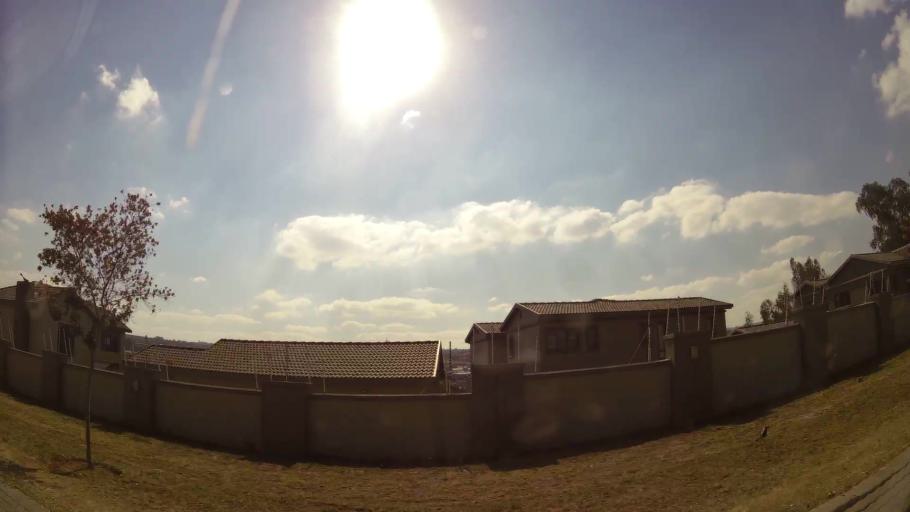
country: ZA
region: Gauteng
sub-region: City of Johannesburg Metropolitan Municipality
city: Midrand
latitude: -26.0081
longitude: 28.0757
